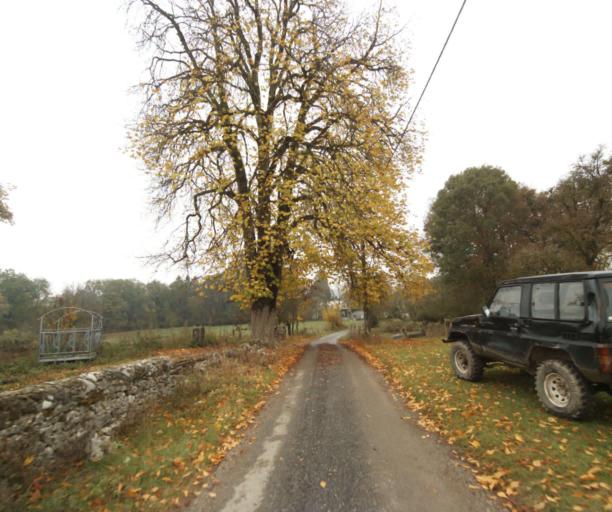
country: FR
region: Rhone-Alpes
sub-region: Departement de la Haute-Savoie
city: Bonne-sur-Menoge
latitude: 46.1391
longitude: 6.3011
